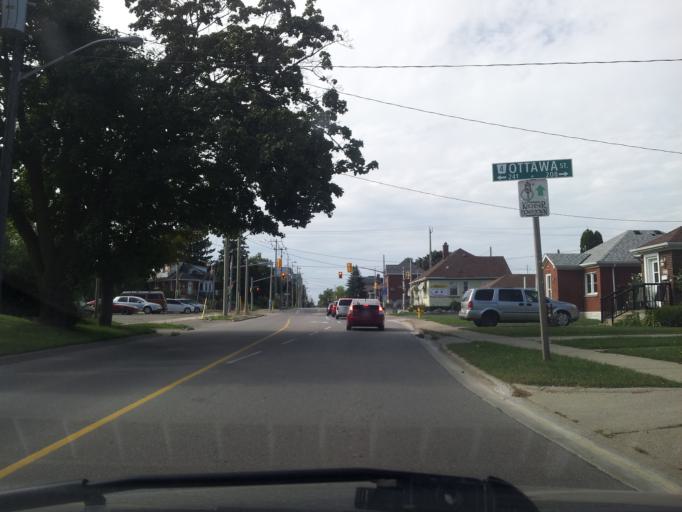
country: CA
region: Ontario
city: Kitchener
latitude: 43.4363
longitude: -80.4761
